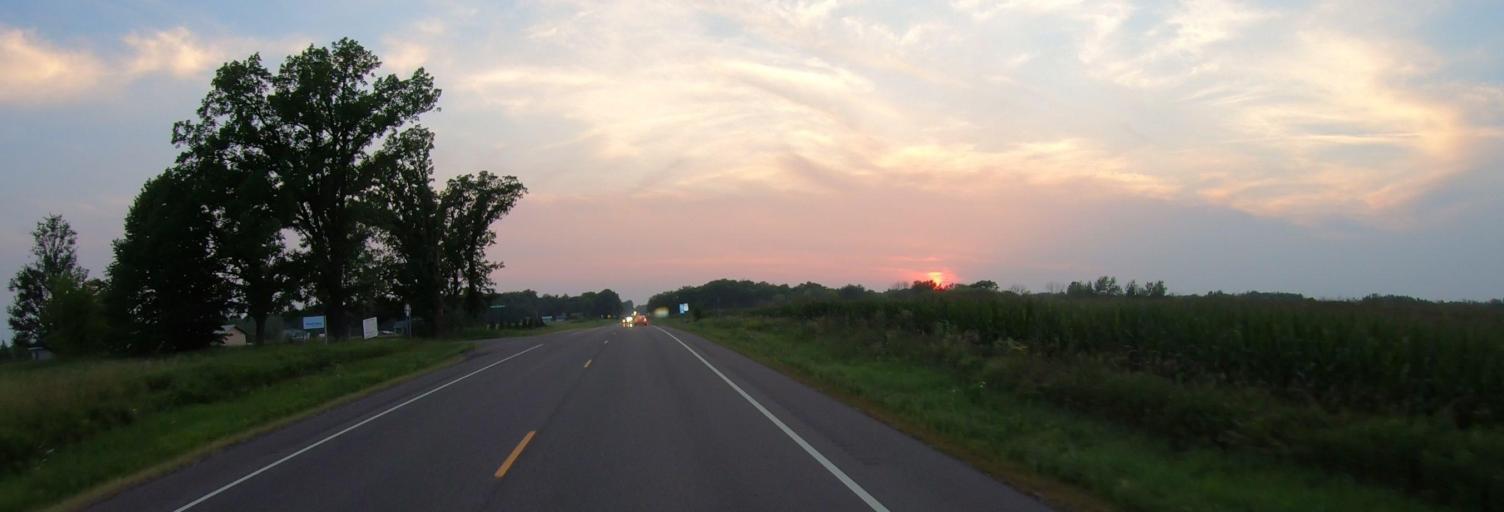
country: US
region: Minnesota
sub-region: Pine County
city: Rock Creek
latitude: 45.7737
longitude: -92.9538
